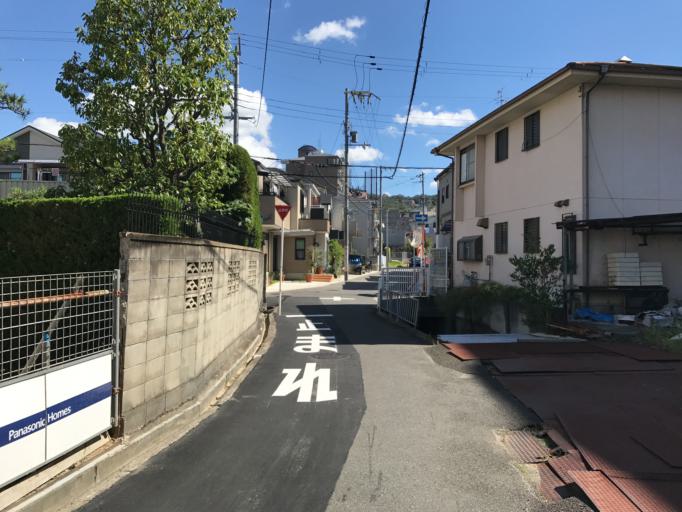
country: JP
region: Osaka
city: Neyagawa
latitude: 34.7435
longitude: 135.6455
